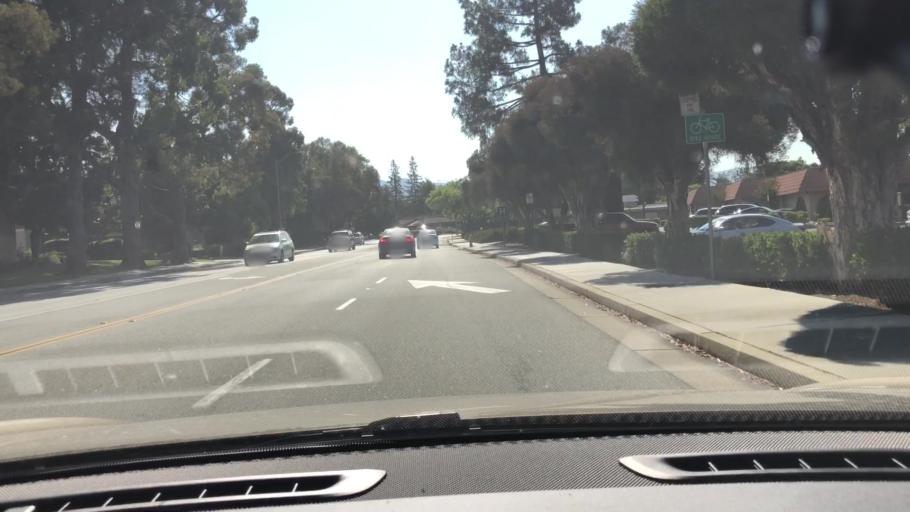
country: US
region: California
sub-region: Santa Clara County
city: Campbell
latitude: 37.2617
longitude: -121.9678
